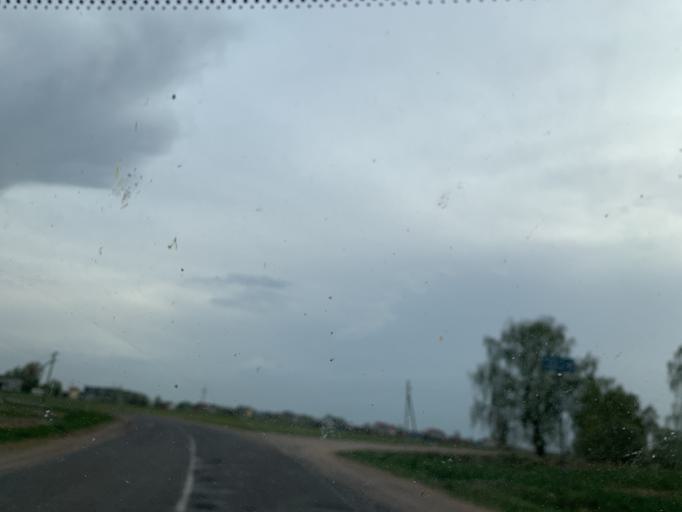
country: BY
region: Minsk
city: Kapyl'
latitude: 53.2679
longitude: 26.9576
